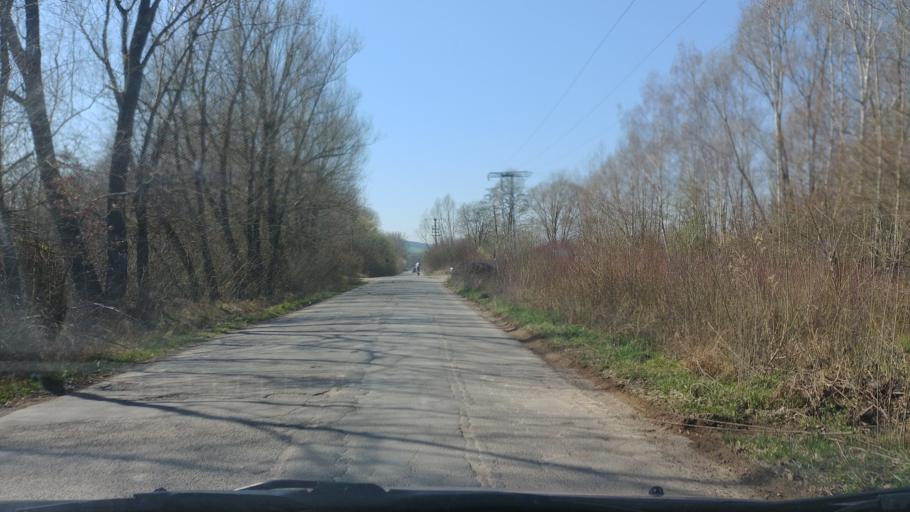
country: DE
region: Lower Saxony
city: Northeim
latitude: 51.7377
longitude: 9.9612
